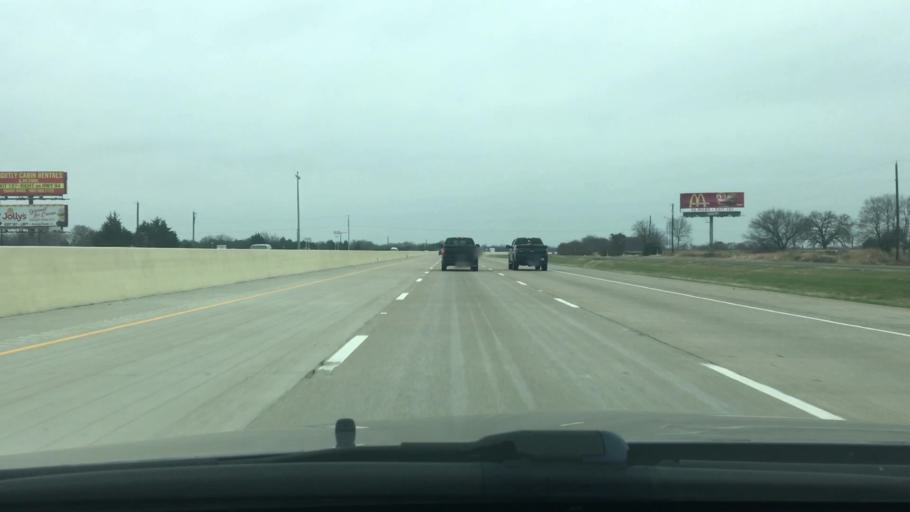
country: US
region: Texas
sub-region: Navarro County
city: Corsicana
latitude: 31.9886
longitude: -96.4257
